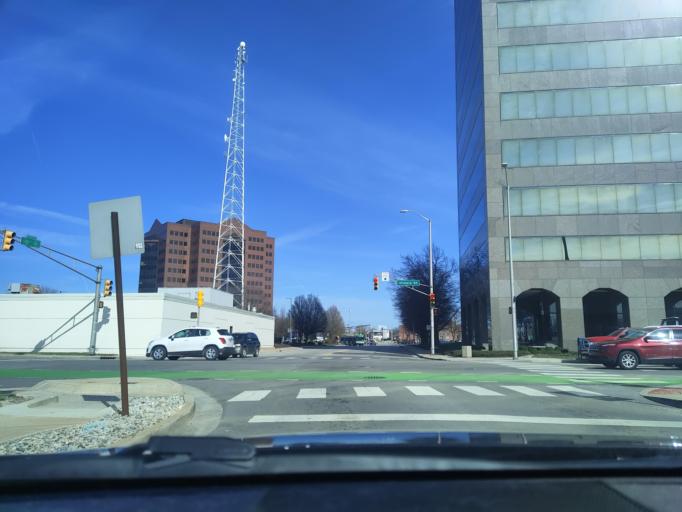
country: US
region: Indiana
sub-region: Marion County
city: Indianapolis
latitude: 39.7811
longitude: -86.1597
